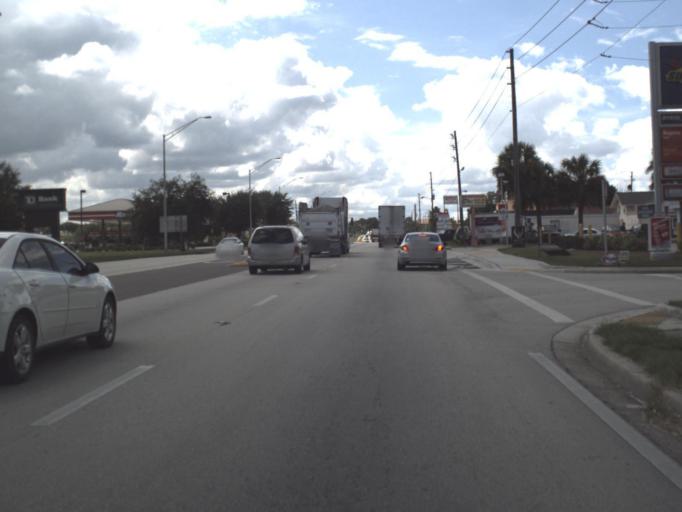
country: US
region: Florida
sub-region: Polk County
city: Lake Wales
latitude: 27.8941
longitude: -81.5578
